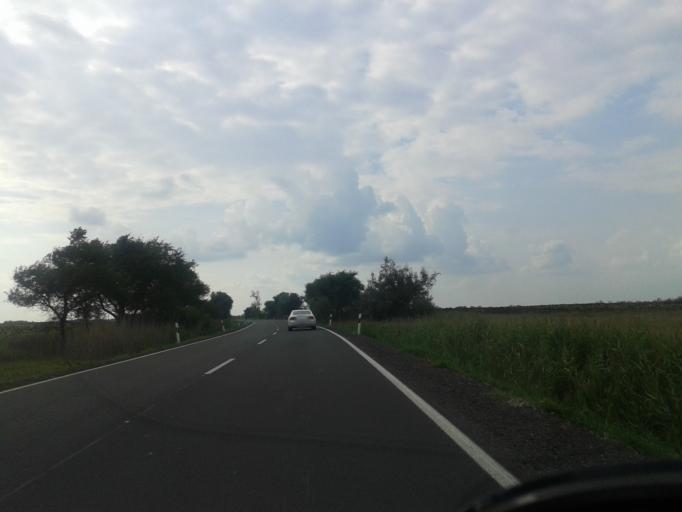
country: HU
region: Bacs-Kiskun
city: Akaszto
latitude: 46.7453
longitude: 19.1379
